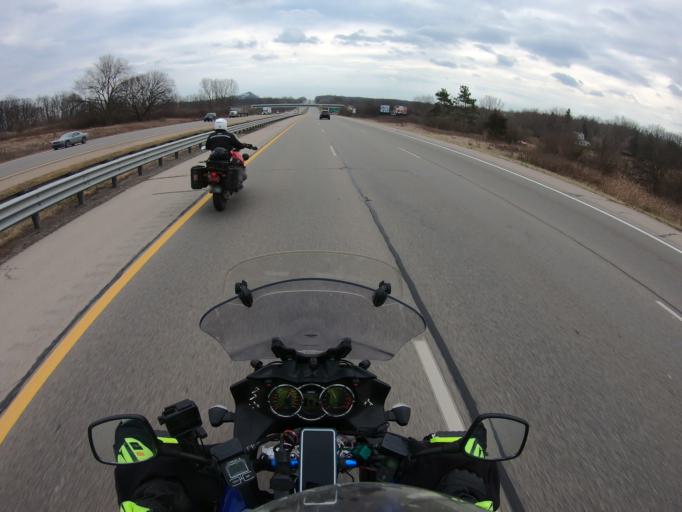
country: US
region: Michigan
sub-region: Oakland County
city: Holly
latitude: 42.8452
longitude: -83.5870
